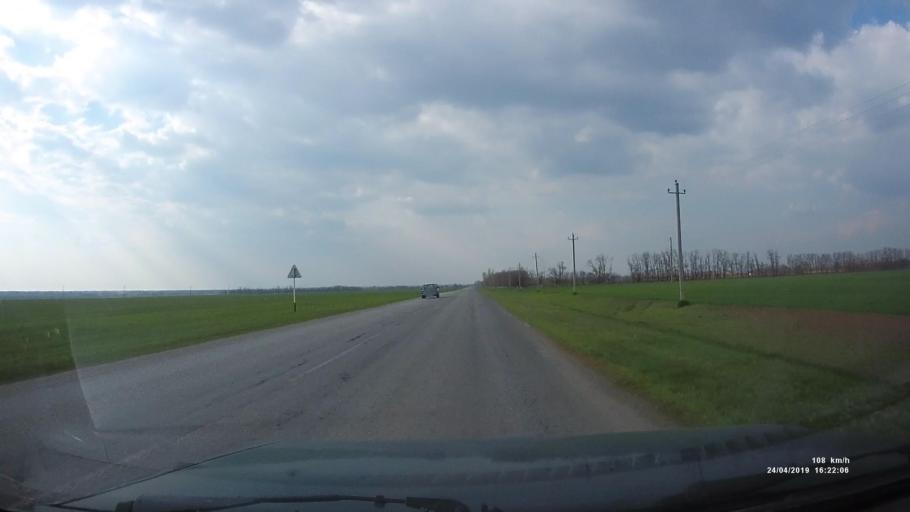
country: RU
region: Rostov
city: Orlovskiy
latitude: 46.8142
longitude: 42.0594
